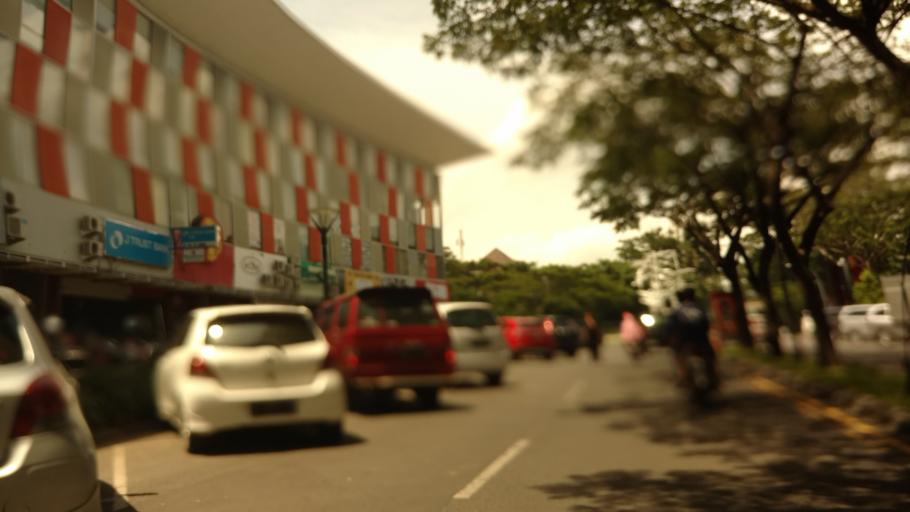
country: ID
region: East Java
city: Driyorejo
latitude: -7.2848
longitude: 112.6567
